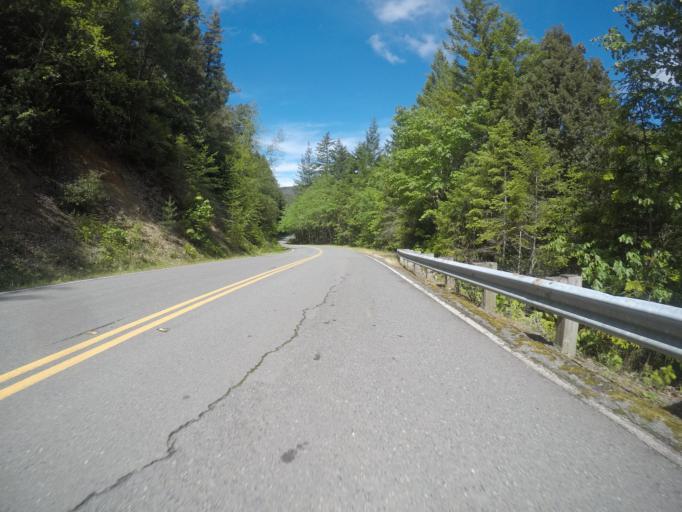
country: US
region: California
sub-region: Del Norte County
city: Bertsch-Oceanview
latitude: 41.7263
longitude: -123.9583
